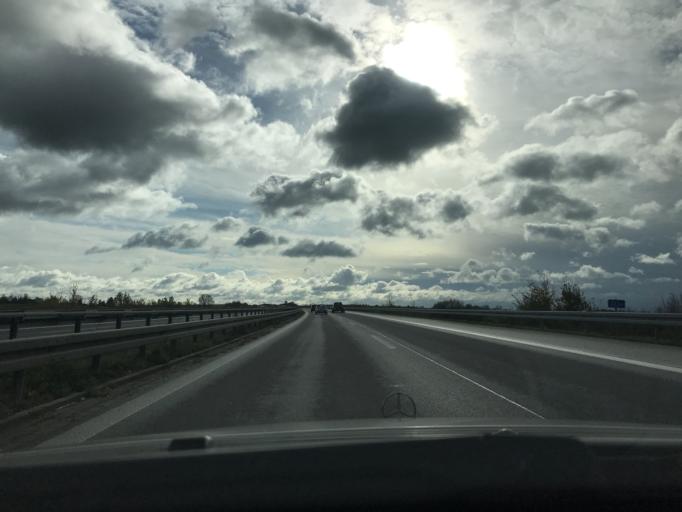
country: DE
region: Brandenburg
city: Grunow
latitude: 53.2934
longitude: 13.9856
